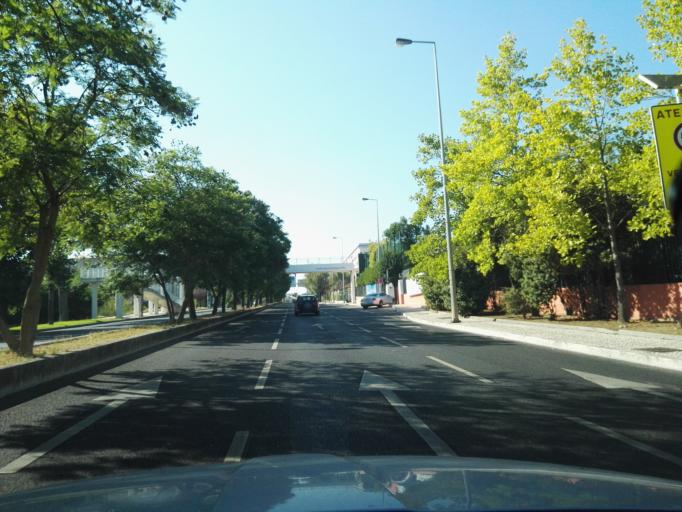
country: PT
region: Lisbon
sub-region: Loures
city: Moscavide
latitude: 38.7786
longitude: -9.1152
